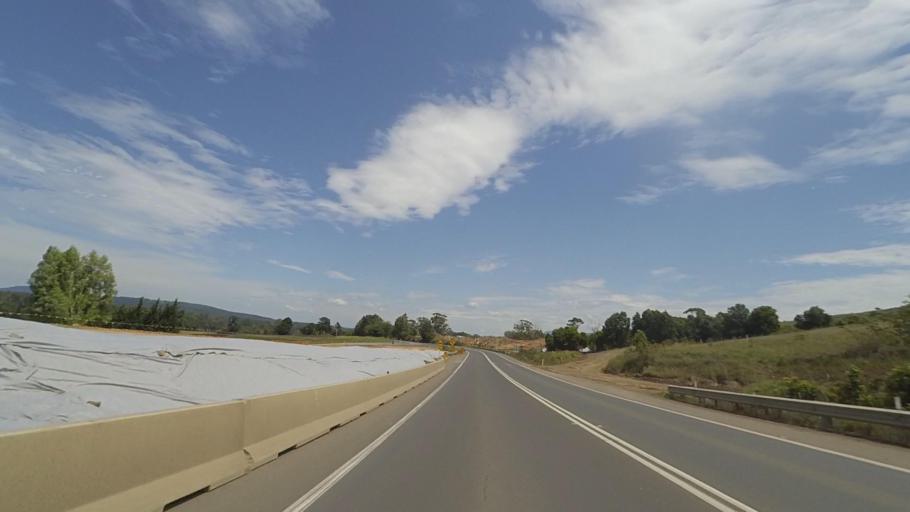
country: AU
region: New South Wales
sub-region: Shoalhaven Shire
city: Berry
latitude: -34.7587
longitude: 150.7422
